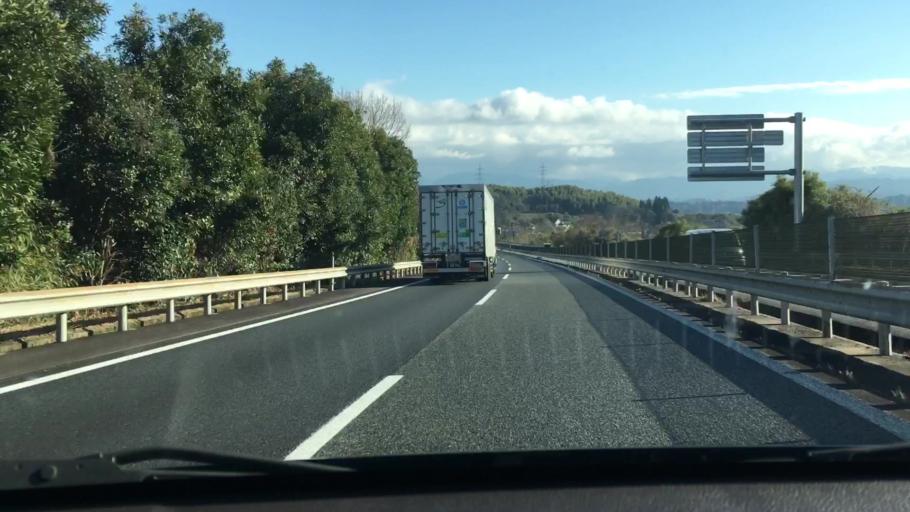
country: JP
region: Kumamoto
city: Hitoyoshi
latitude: 32.2385
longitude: 130.7615
